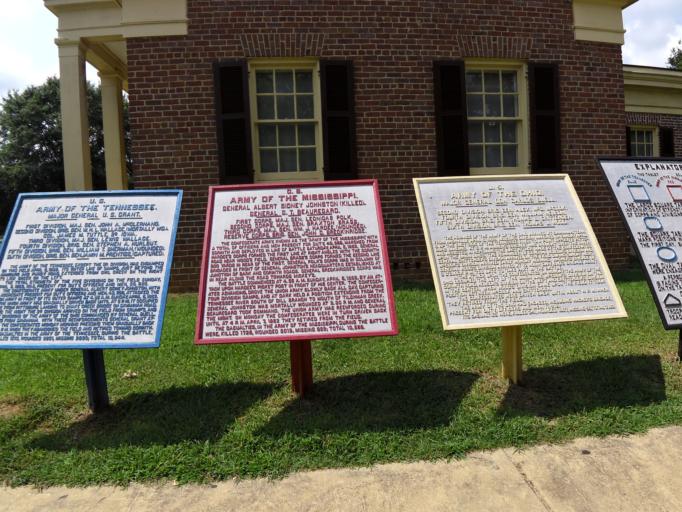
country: US
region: Tennessee
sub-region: Hardin County
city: Crump
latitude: 35.1512
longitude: -88.3221
